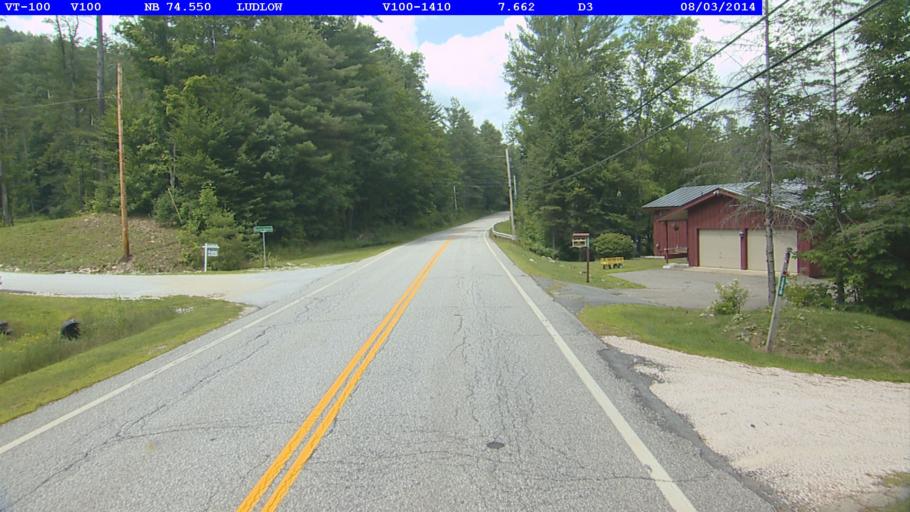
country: US
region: Vermont
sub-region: Windsor County
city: Chester
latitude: 43.4533
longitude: -72.7066
